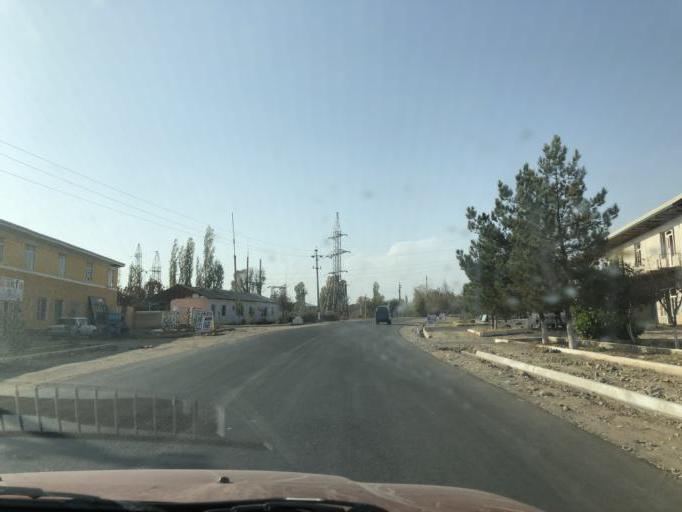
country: UZ
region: Namangan
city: Chust Shahri
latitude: 41.0741
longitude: 71.2007
